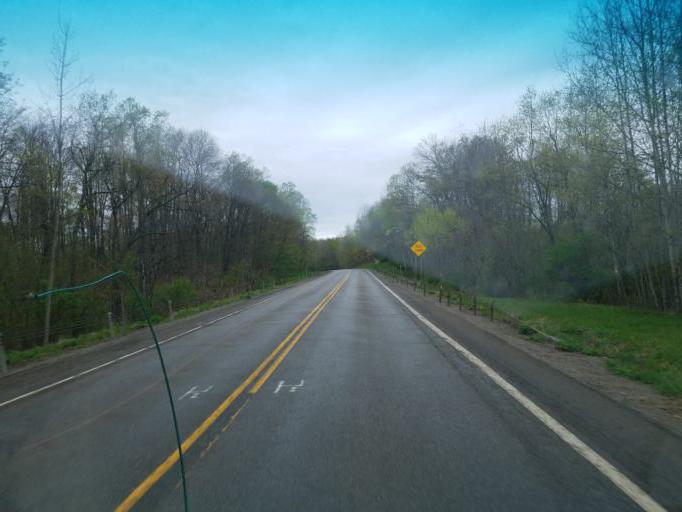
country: US
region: New York
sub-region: Allegany County
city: Wellsville
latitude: 42.0028
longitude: -77.8561
